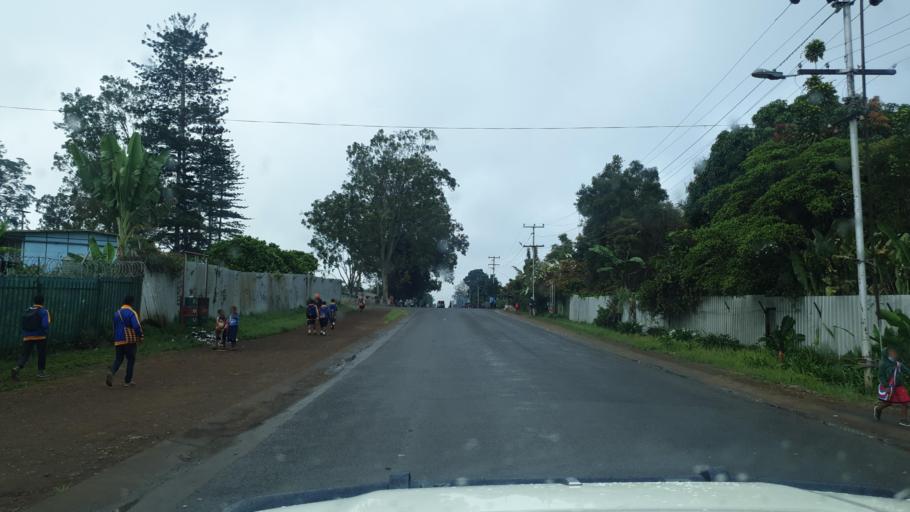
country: PG
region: Eastern Highlands
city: Goroka
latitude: -6.0777
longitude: 145.3873
